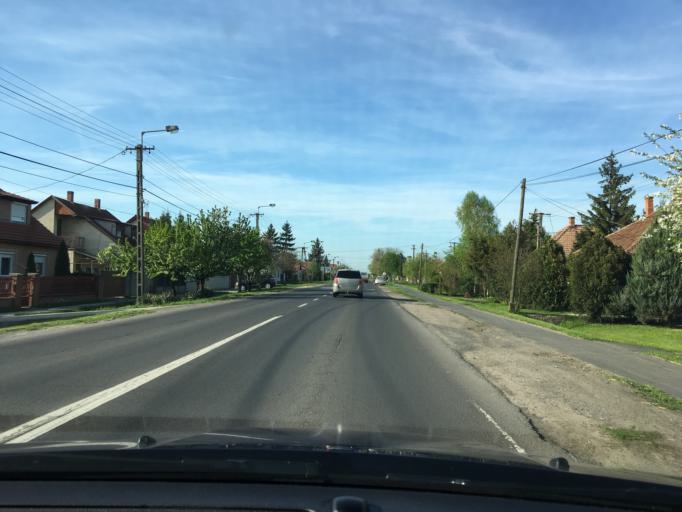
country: HU
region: Bekes
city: Mezobereny
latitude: 46.8358
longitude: 21.0275
